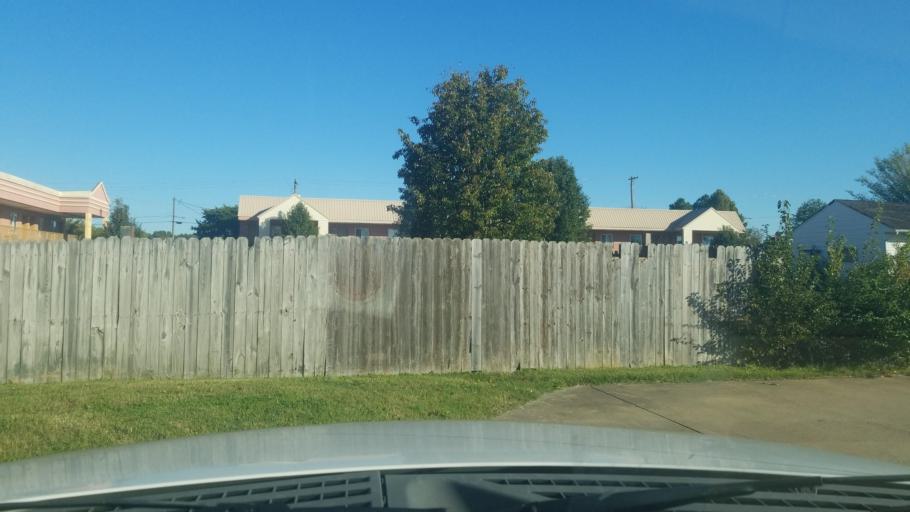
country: US
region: Illinois
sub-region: Williamson County
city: Marion
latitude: 37.7419
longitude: -88.9486
